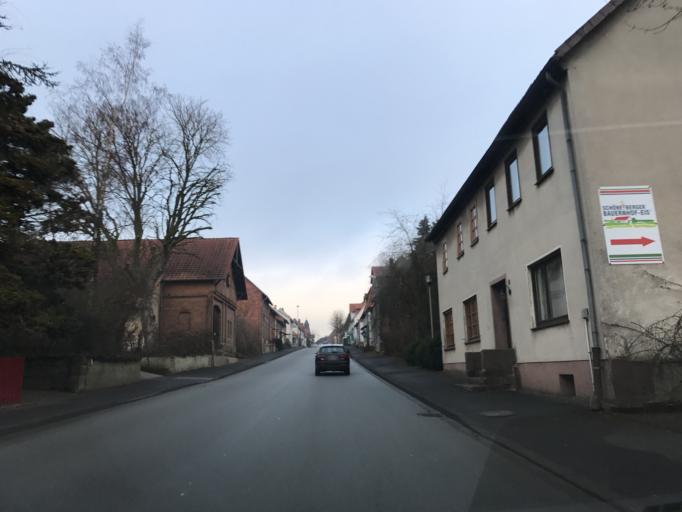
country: DE
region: Hesse
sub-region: Regierungsbezirk Kassel
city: Hofgeismar
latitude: 51.5173
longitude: 9.4182
